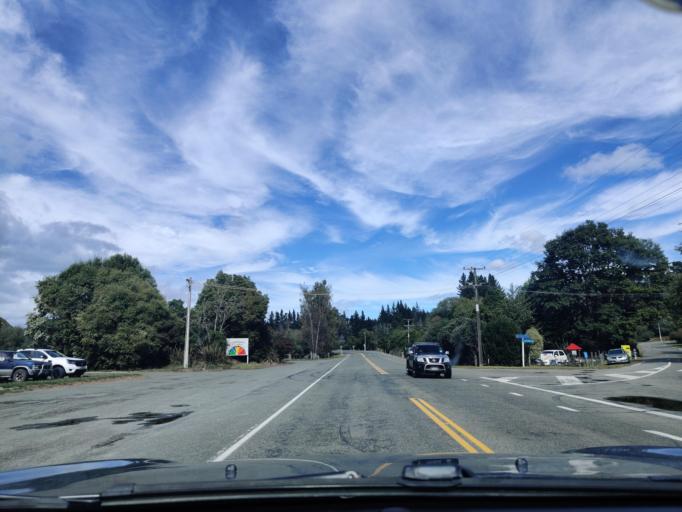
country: NZ
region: Tasman
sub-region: Tasman District
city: Wakefield
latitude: -41.4492
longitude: 172.9598
